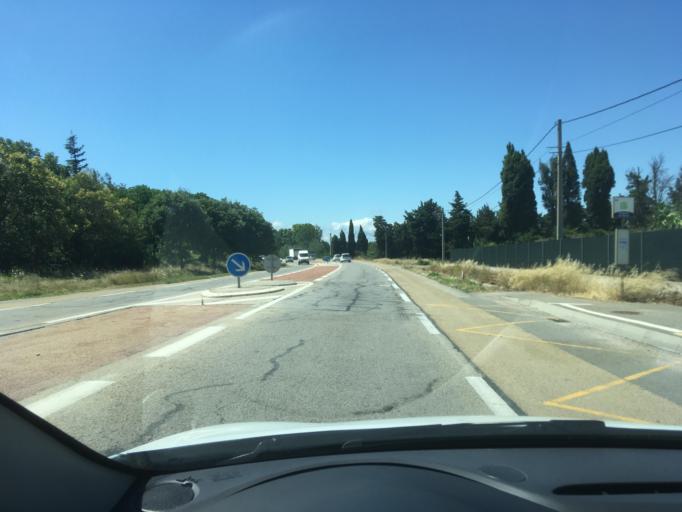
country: FR
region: Provence-Alpes-Cote d'Azur
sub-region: Departement des Bouches-du-Rhone
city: Rognonas
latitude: 43.8927
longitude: 4.8294
